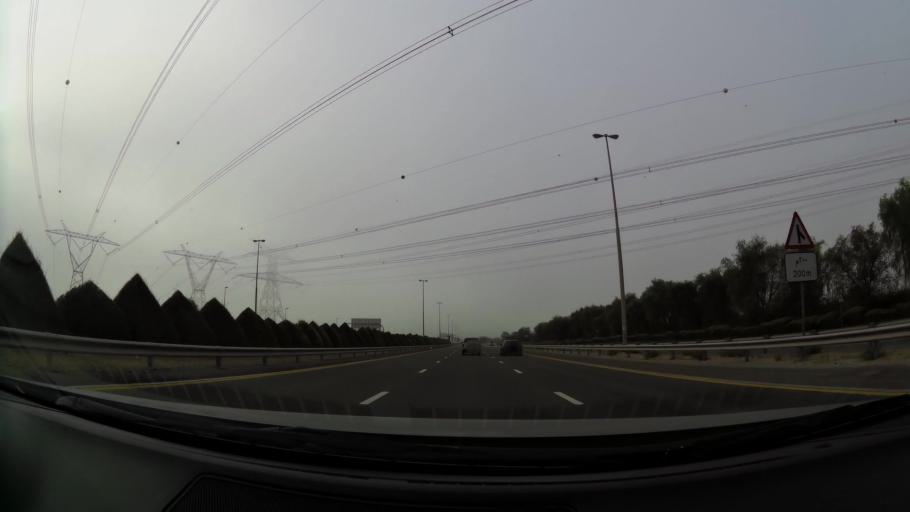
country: AE
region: Dubai
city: Dubai
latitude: 25.1692
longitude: 55.3253
